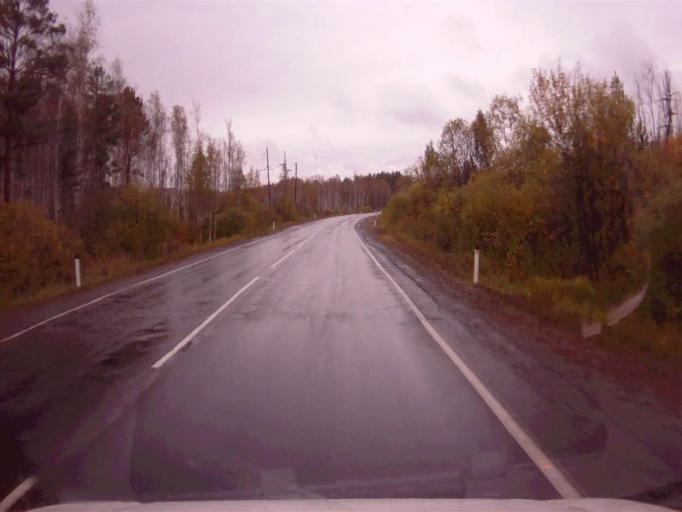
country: RU
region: Chelyabinsk
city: Verkhniy Ufaley
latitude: 55.9917
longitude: 60.3334
